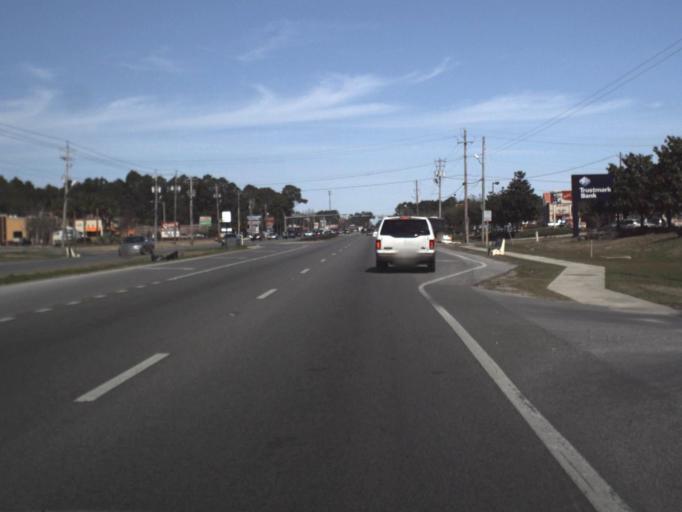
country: US
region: Florida
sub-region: Bay County
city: Lynn Haven
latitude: 30.2231
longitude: -85.6492
